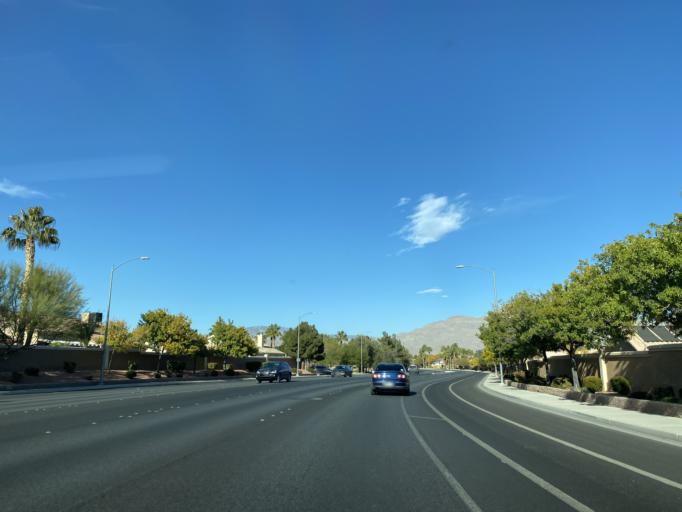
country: US
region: Nevada
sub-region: Clark County
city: Las Vegas
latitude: 36.2916
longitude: -115.2602
